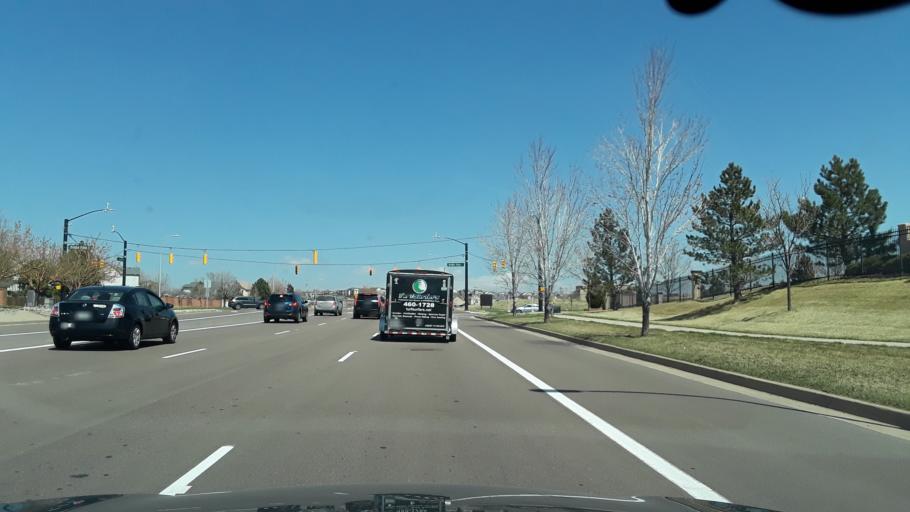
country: US
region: Colorado
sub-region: El Paso County
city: Cimarron Hills
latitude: 38.9350
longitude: -104.7403
